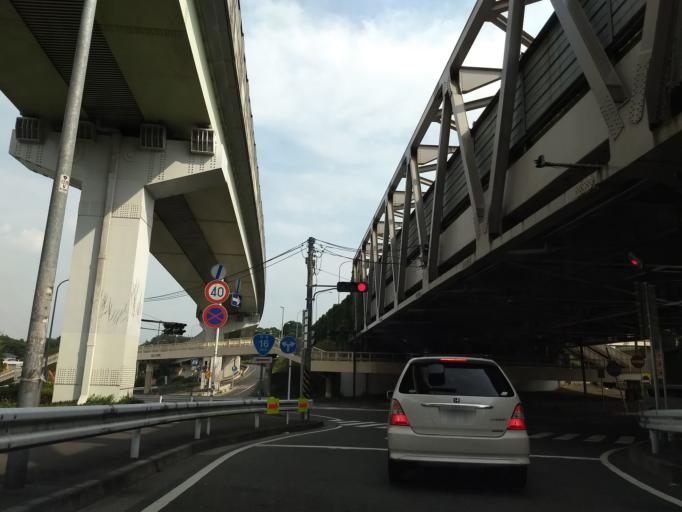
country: JP
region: Kanagawa
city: Minami-rinkan
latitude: 35.4984
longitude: 139.4934
